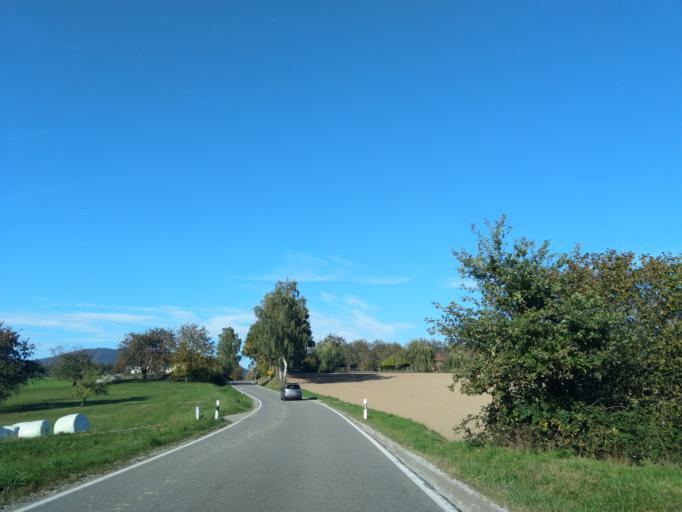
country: DE
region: Bavaria
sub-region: Lower Bavaria
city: Bernried
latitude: 48.8937
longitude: 12.9010
